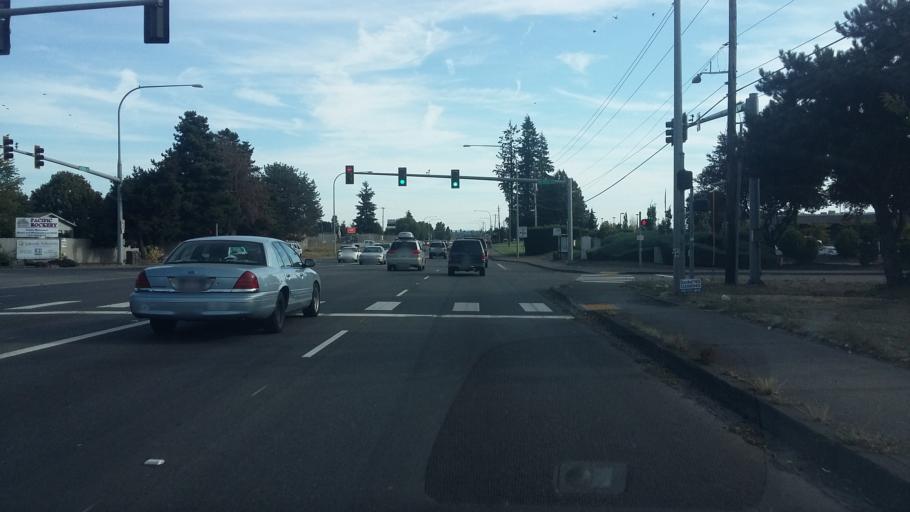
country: US
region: Washington
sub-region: Clark County
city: Orchards
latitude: 45.6860
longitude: -122.5527
